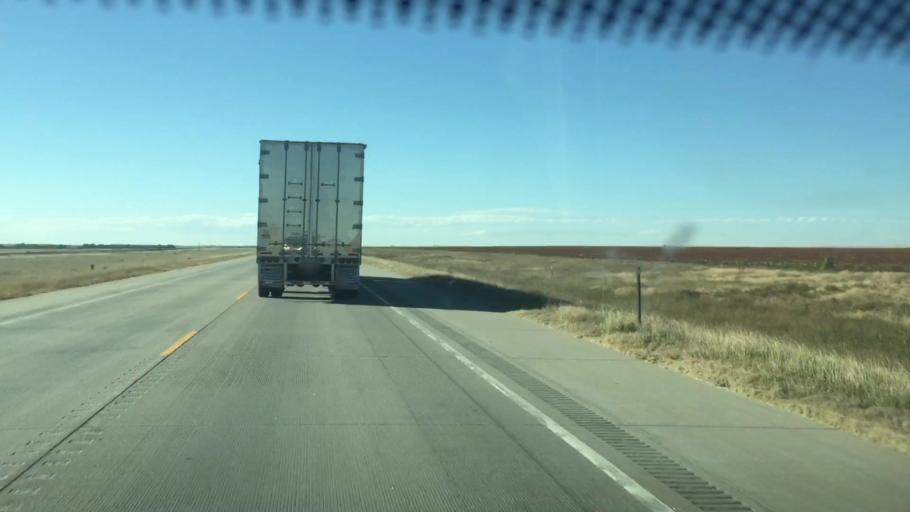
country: US
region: Colorado
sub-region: Kiowa County
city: Eads
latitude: 38.7960
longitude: -102.9466
